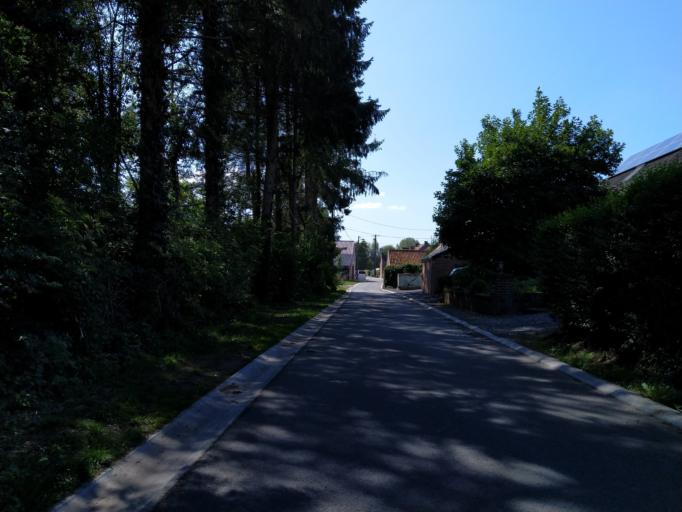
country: BE
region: Wallonia
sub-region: Province du Hainaut
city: Jurbise
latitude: 50.5305
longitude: 3.8827
